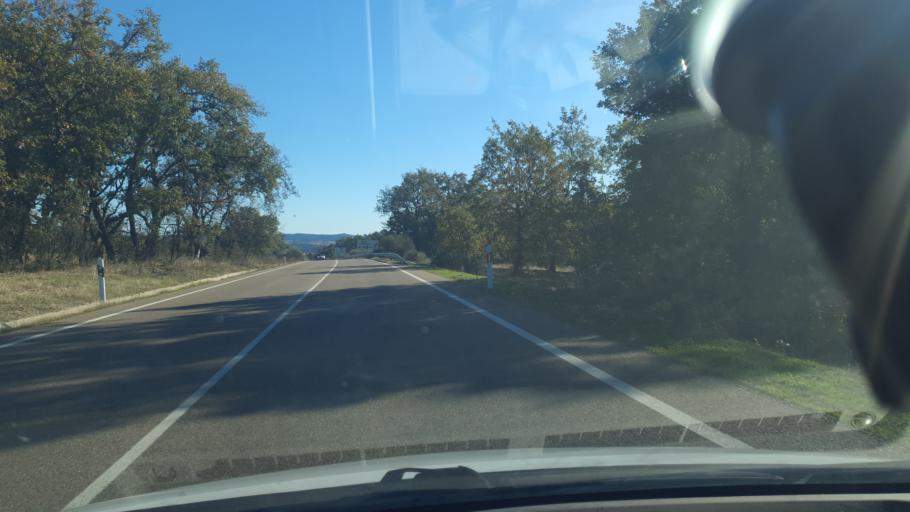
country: ES
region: Castille and Leon
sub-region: Provincia de Avila
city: Candeleda
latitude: 40.1356
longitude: -5.2342
